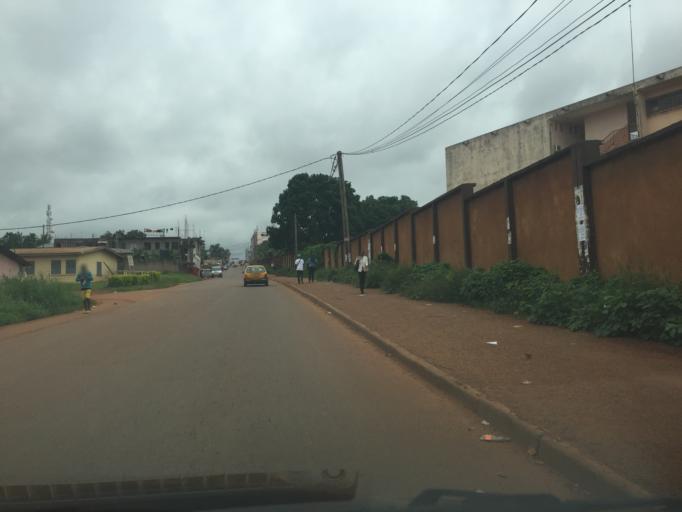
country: CM
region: Centre
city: Yaounde
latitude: 3.8549
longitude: 11.5070
